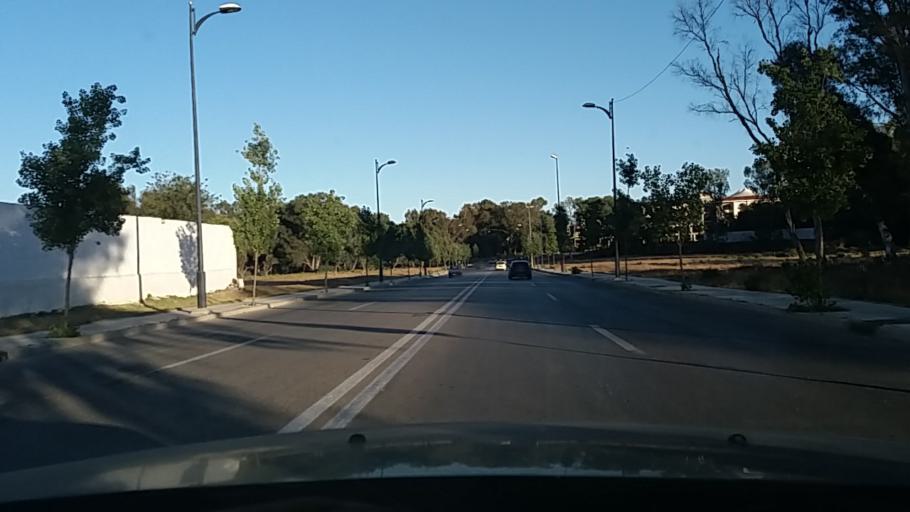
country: MA
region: Tanger-Tetouan
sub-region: Tanger-Assilah
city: Tangier
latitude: 35.7753
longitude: -5.8583
